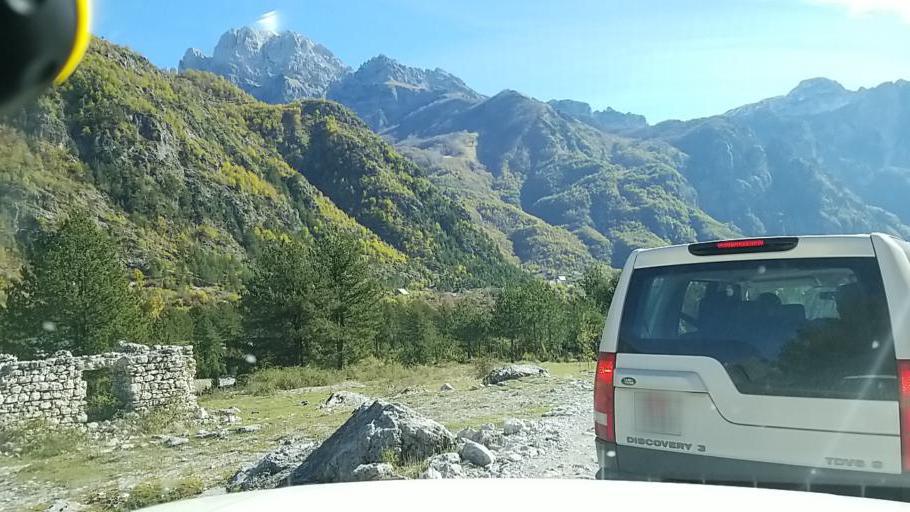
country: AL
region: Shkoder
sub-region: Rrethi i Shkodres
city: Nicaj-Shale
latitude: 42.3941
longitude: 19.7737
